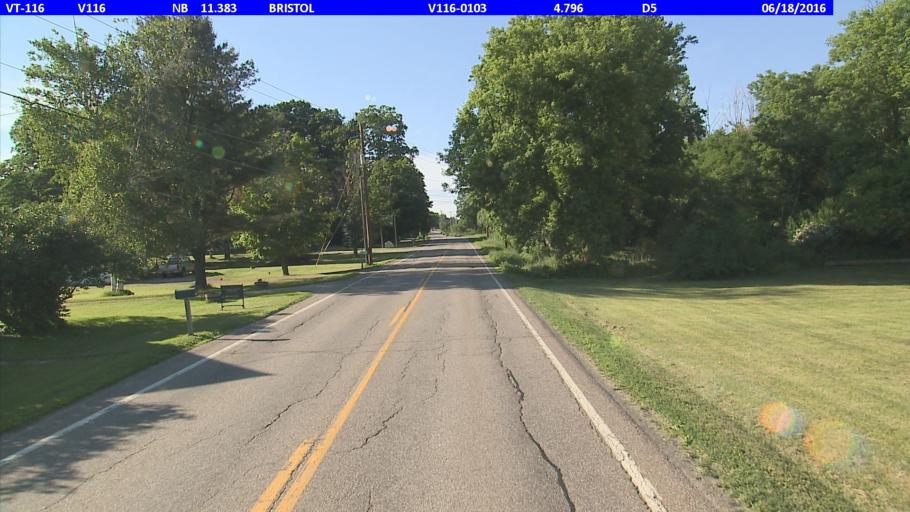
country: US
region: Vermont
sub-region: Addison County
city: Bristol
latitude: 44.1197
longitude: -73.0963
